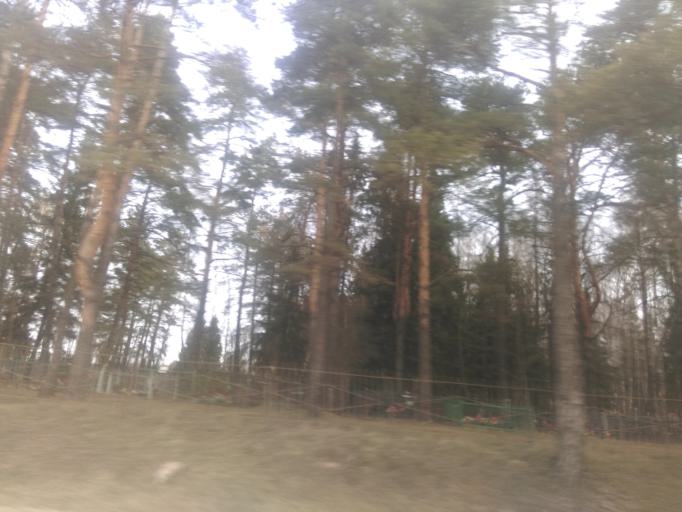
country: RU
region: Moskovskaya
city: Tuchkovo
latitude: 55.5667
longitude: 36.5201
